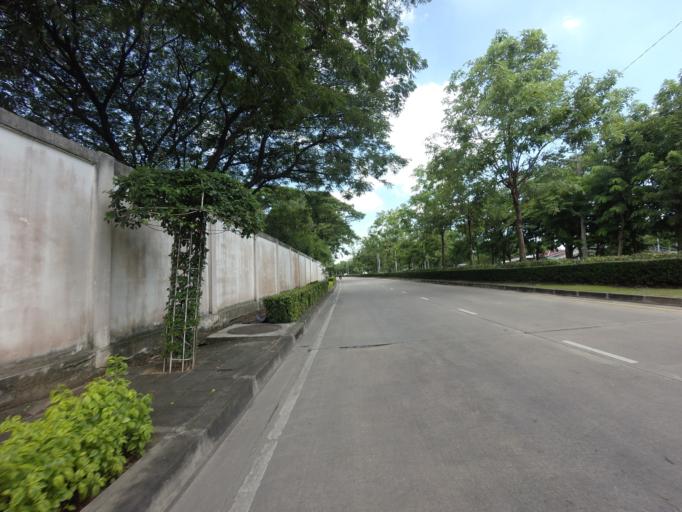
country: TH
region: Bangkok
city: Chatuchak
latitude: 13.8470
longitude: 100.5890
